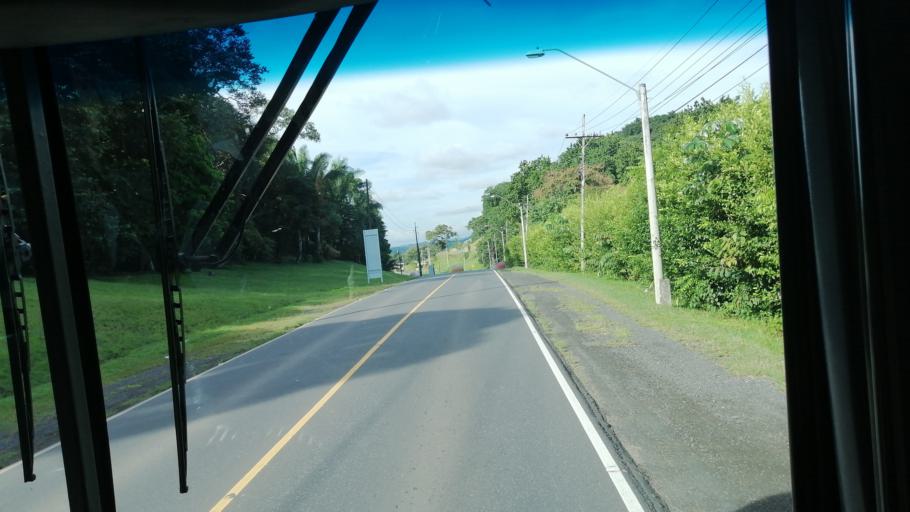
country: PA
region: Panama
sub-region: Distrito de Panama
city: Ancon
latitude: 8.9459
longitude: -79.5913
